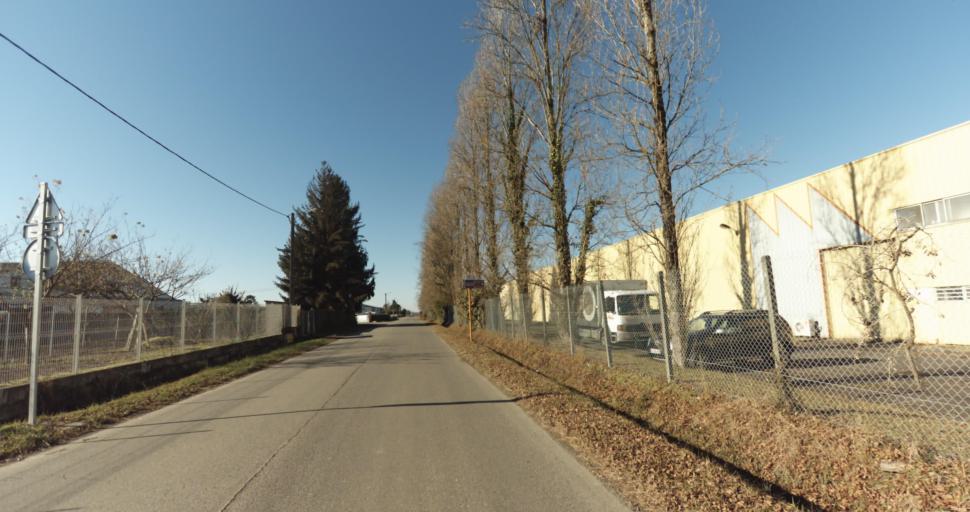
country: FR
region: Aquitaine
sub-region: Departement des Pyrenees-Atlantiques
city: Buros
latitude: 43.3288
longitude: -0.3003
